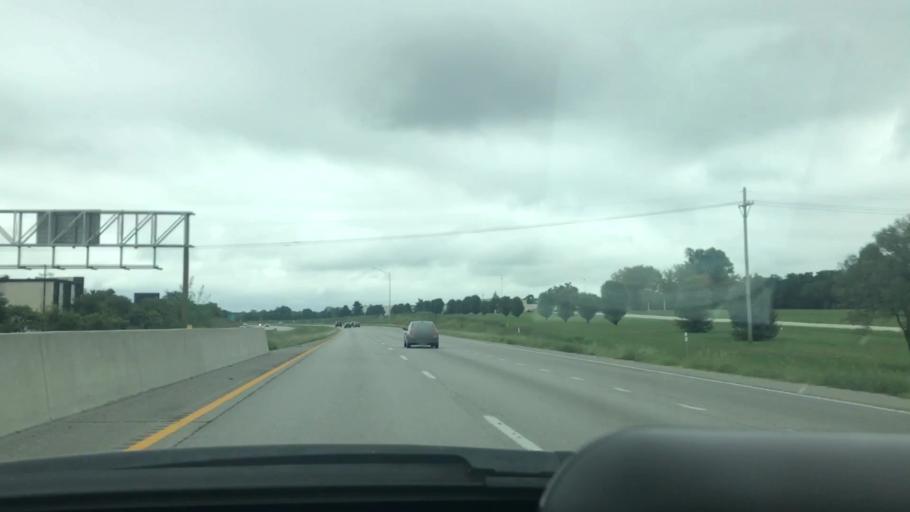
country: US
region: Missouri
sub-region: Jasper County
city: Duquesne
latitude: 37.0466
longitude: -94.4747
